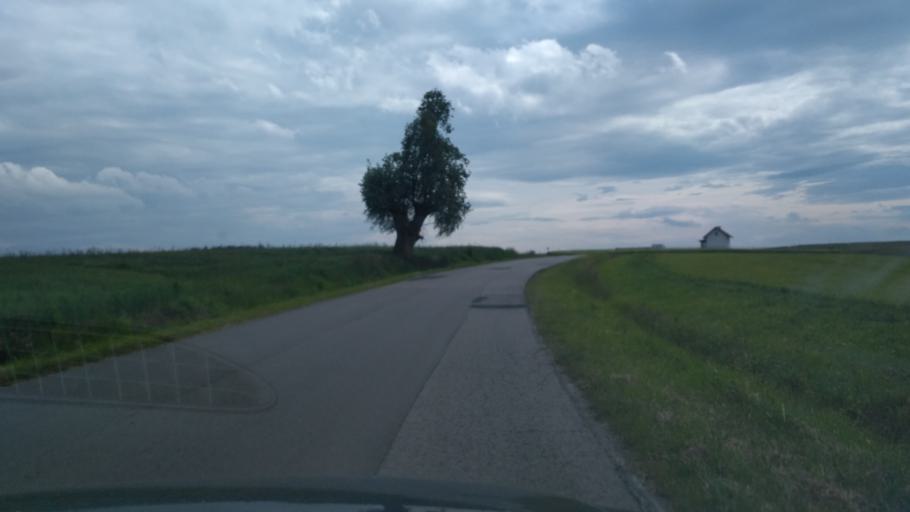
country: PL
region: Subcarpathian Voivodeship
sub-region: Powiat ropczycko-sedziszowski
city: Wielopole Skrzynskie
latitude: 49.9985
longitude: 21.6134
